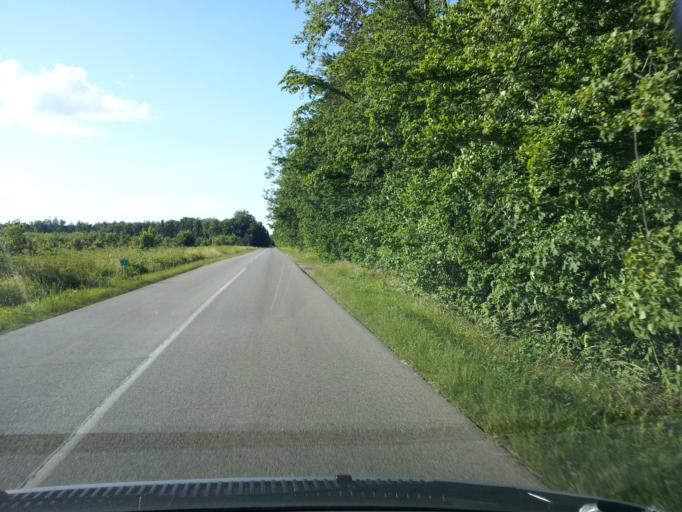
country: HU
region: Veszprem
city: Zirc
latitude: 47.2382
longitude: 17.8586
